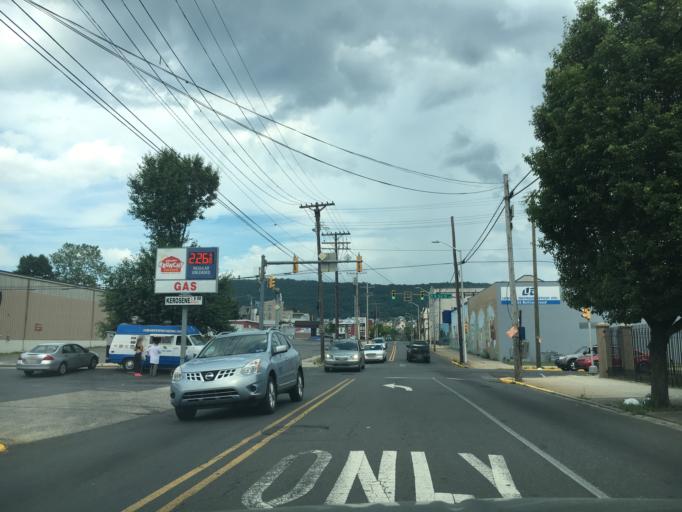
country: US
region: Pennsylvania
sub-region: Berks County
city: Reading
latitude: 40.3416
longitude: -75.9321
